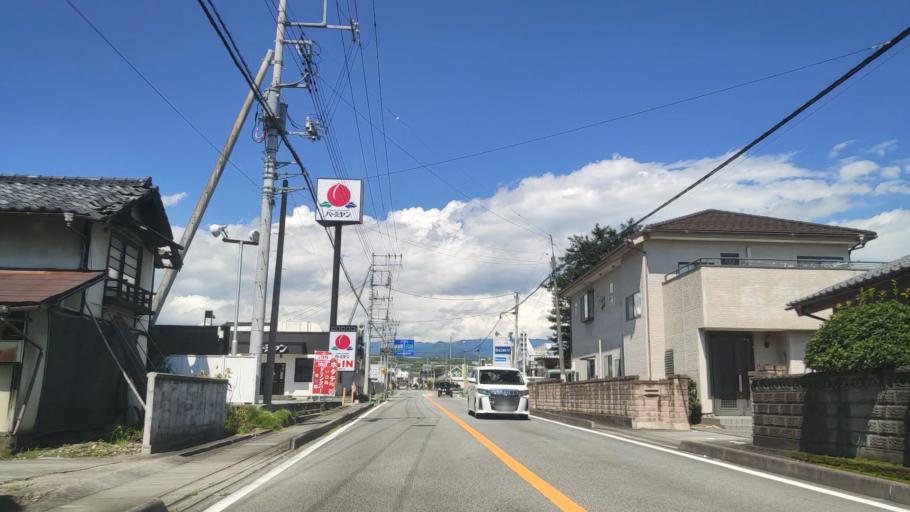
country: JP
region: Yamanashi
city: Isawa
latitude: 35.6798
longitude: 138.6598
